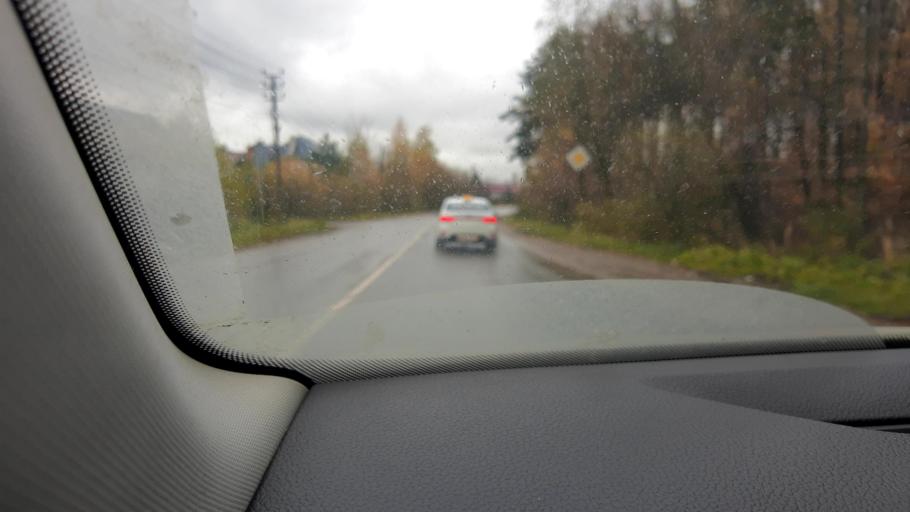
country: RU
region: Moskovskaya
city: Aprelevka
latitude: 55.5543
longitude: 37.0885
